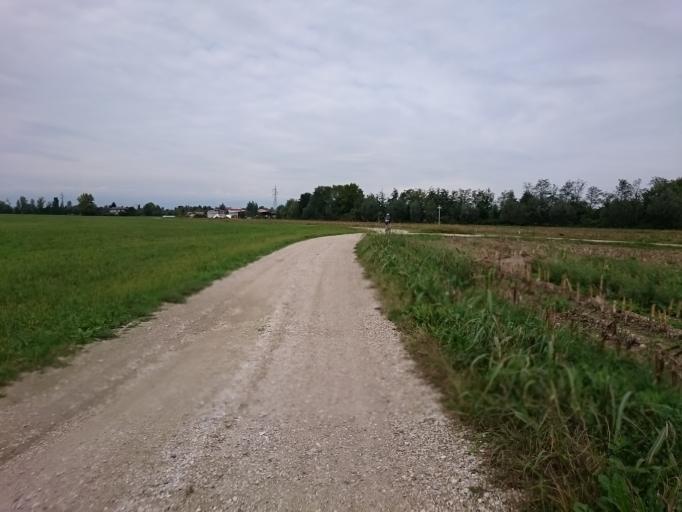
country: IT
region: Veneto
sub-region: Provincia di Vicenza
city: Quinto Vicentino
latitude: 45.5675
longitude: 11.6658
